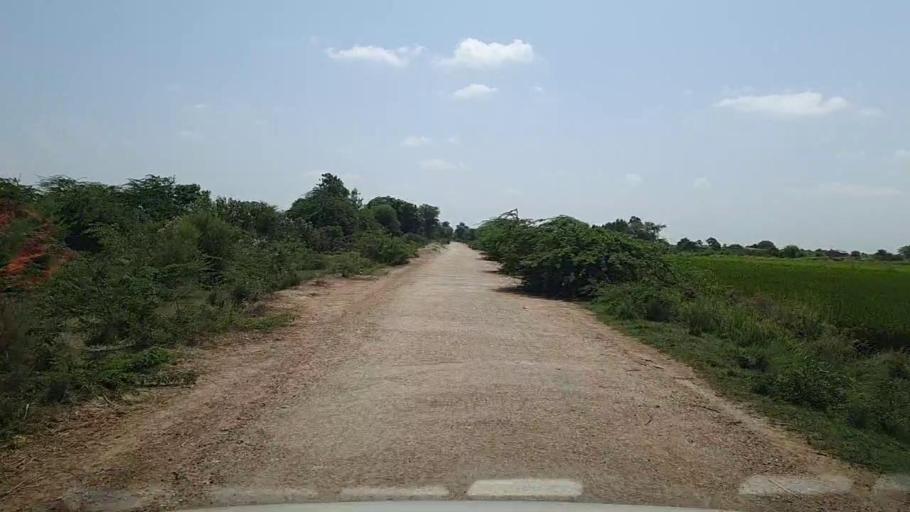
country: PK
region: Sindh
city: Kario
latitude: 24.8697
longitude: 68.6876
